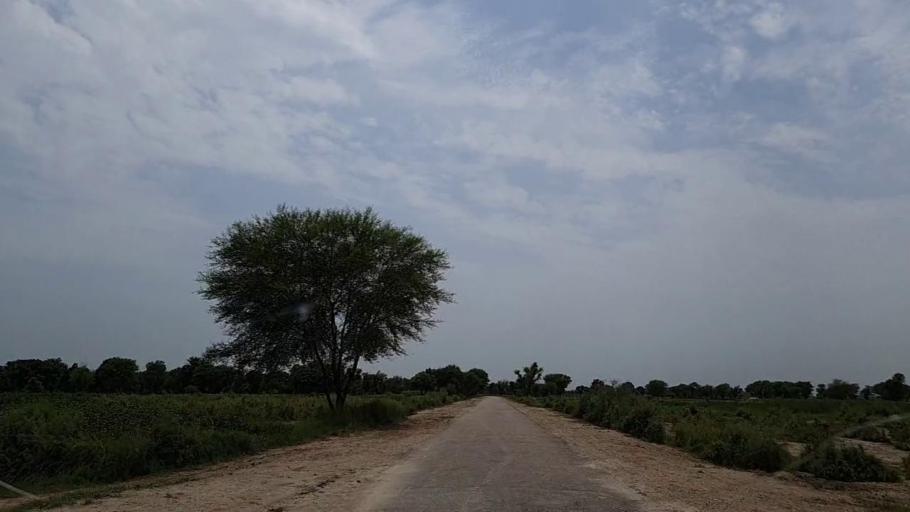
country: PK
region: Sindh
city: Tharu Shah
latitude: 26.9147
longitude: 68.0954
